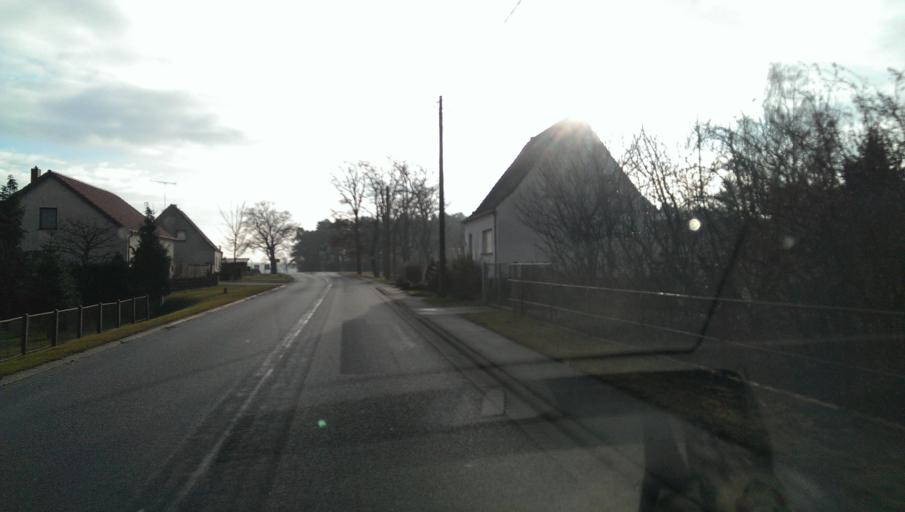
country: DE
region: Saxony-Anhalt
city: Holzdorf
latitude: 51.7967
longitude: 13.1785
